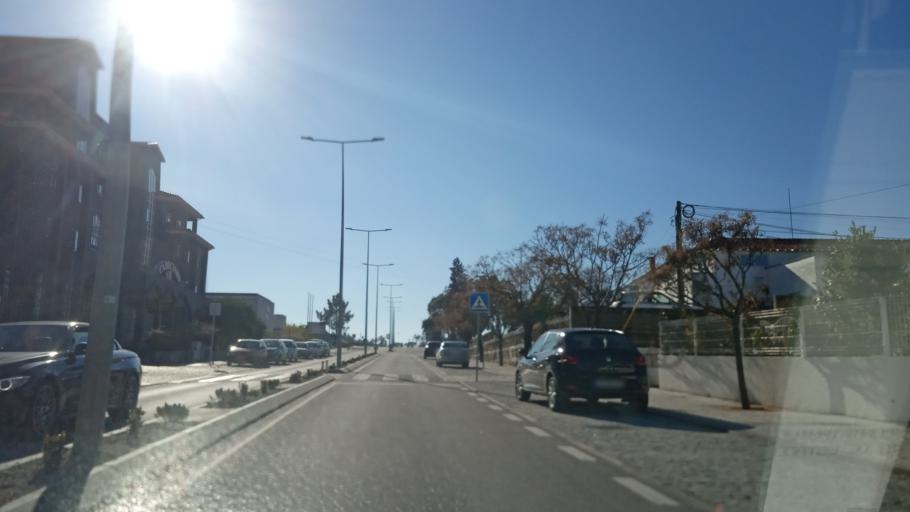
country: PT
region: Aveiro
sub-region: Anadia
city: Anadia
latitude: 40.4373
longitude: -8.4392
